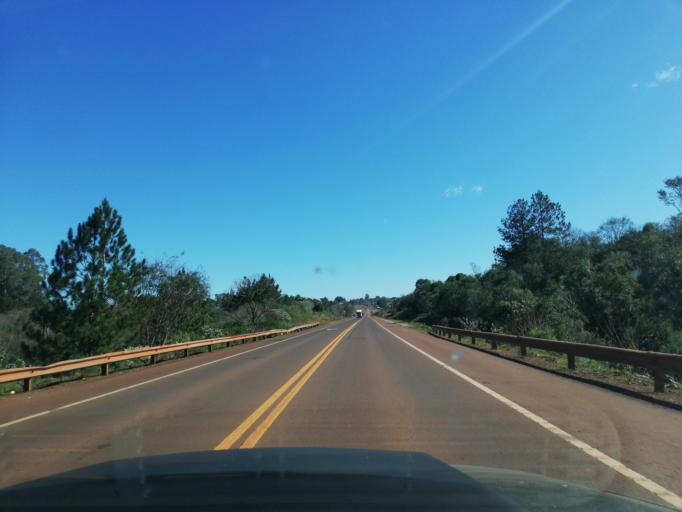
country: AR
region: Misiones
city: Aristobulo del Valle
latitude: -27.0988
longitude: -54.8769
